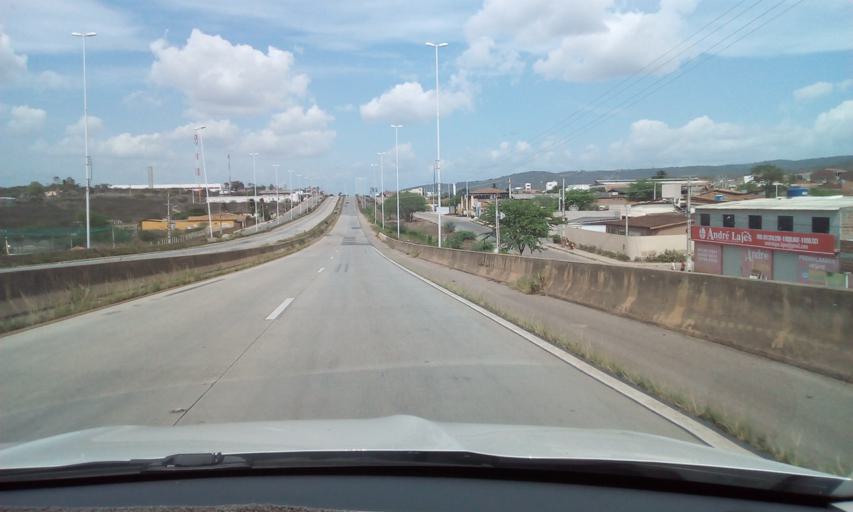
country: BR
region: Pernambuco
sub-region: Bezerros
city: Bezerros
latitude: -8.2377
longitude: -35.7403
